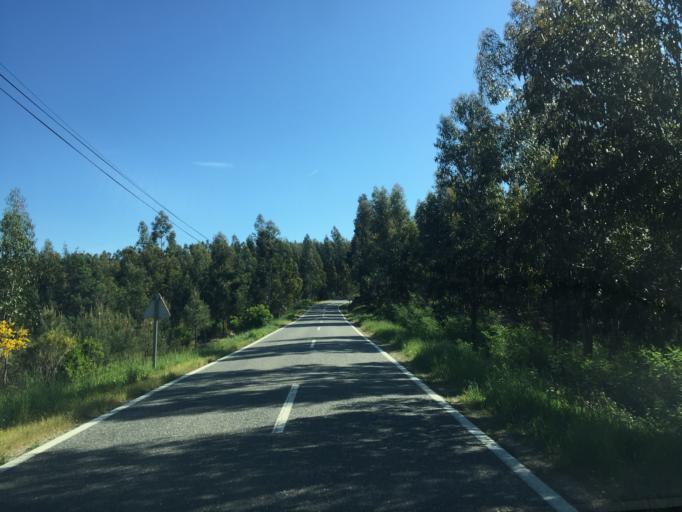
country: PT
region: Coimbra
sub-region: Pampilhosa da Serra
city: Pampilhosa da Serra
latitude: 40.0536
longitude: -7.8662
